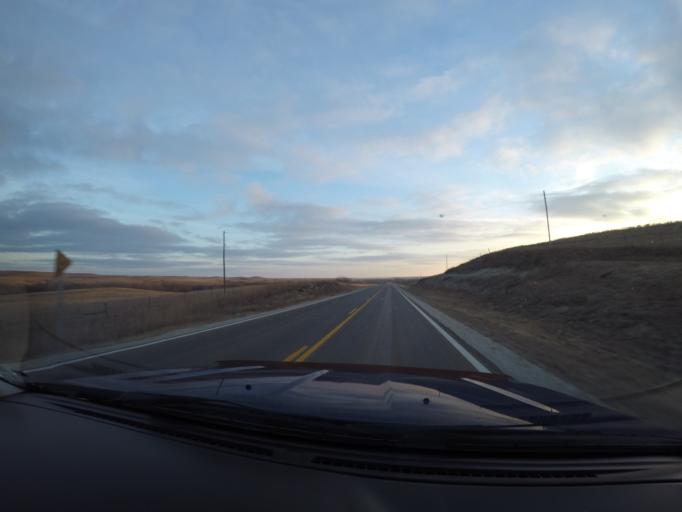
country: US
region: Kansas
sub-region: Chase County
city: Cottonwood Falls
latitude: 38.4917
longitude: -96.5573
